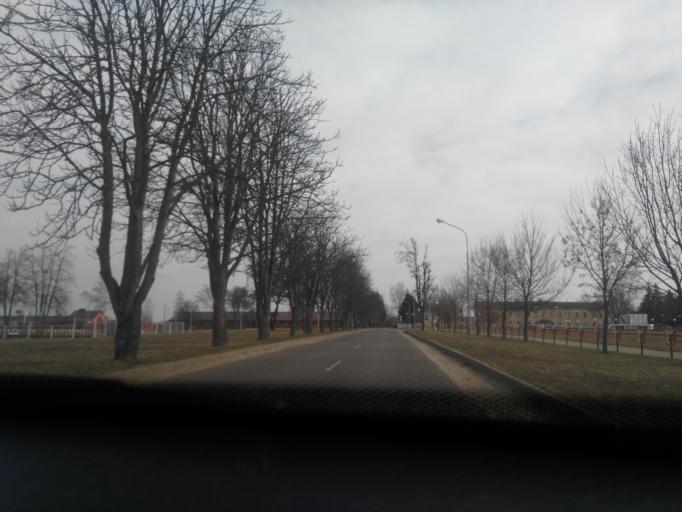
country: BY
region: Mogilev
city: Babruysk
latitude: 53.1407
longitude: 29.2445
